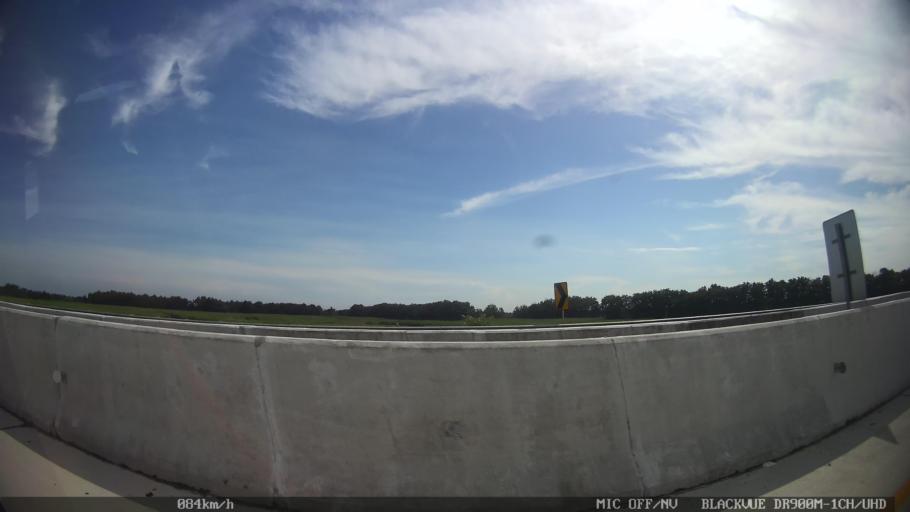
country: ID
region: North Sumatra
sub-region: Kabupaten Langkat
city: Stabat
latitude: 3.7073
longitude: 98.5362
